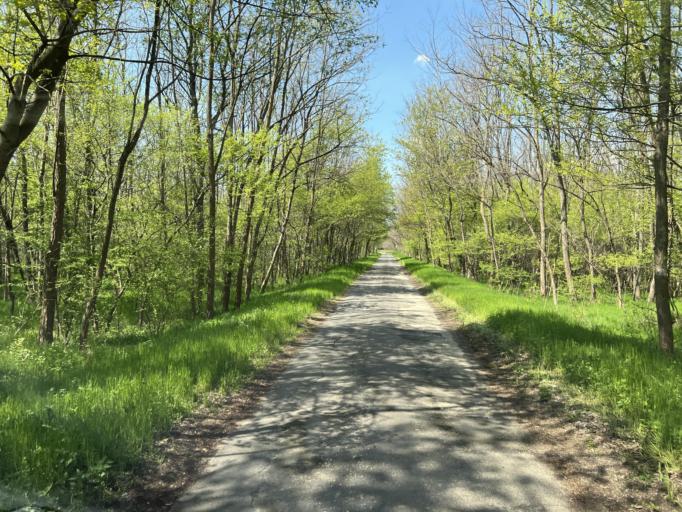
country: HU
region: Pest
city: Kakucs
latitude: 47.2716
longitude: 19.3596
